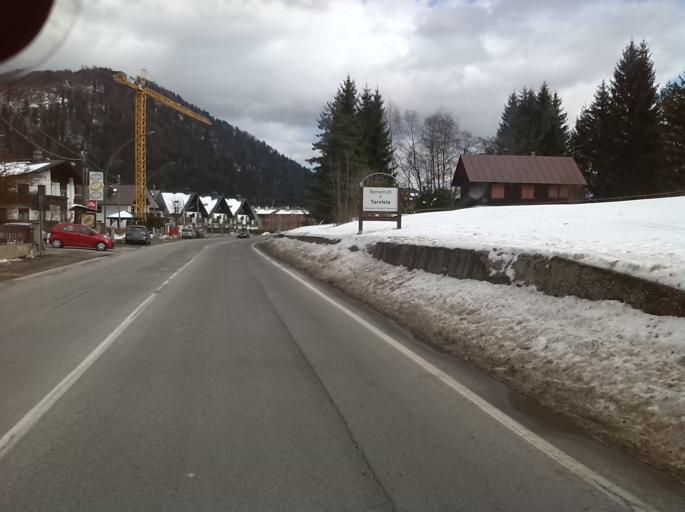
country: IT
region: Friuli Venezia Giulia
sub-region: Provincia di Udine
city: Tarvisio
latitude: 46.5067
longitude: 13.5557
